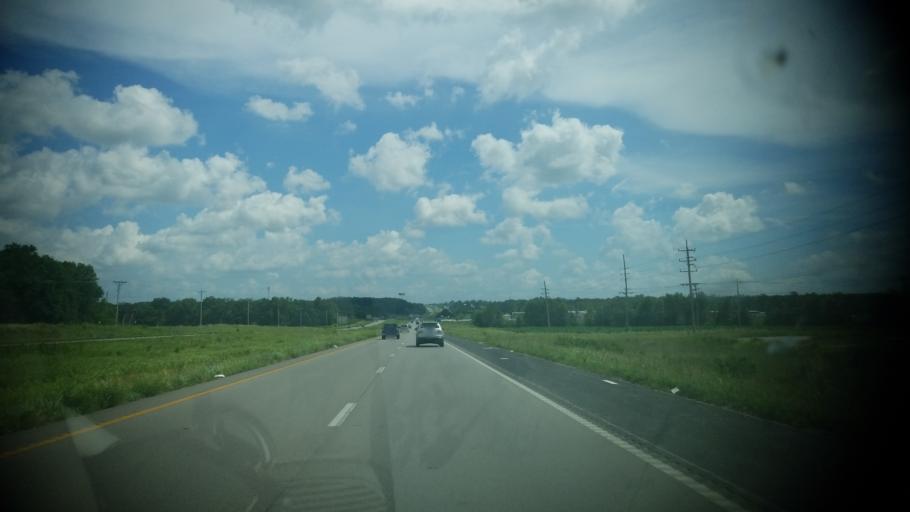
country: US
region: Missouri
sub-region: Lincoln County
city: Moscow Mills
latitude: 38.9375
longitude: -90.9260
